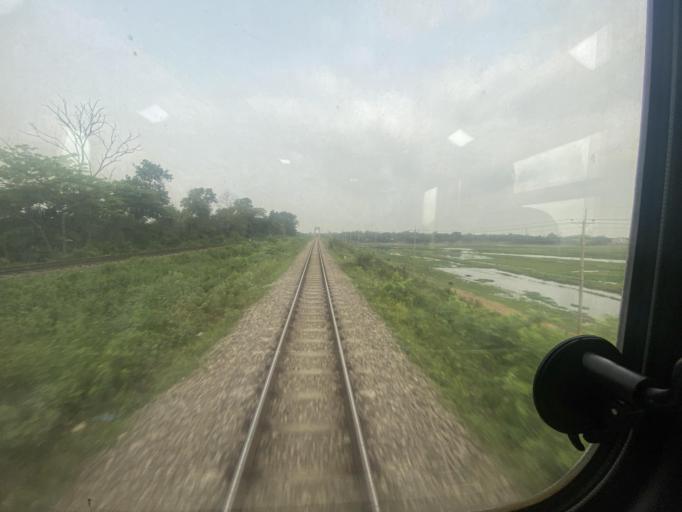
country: BD
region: Dhaka
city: Tungi
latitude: 23.9343
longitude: 90.4928
